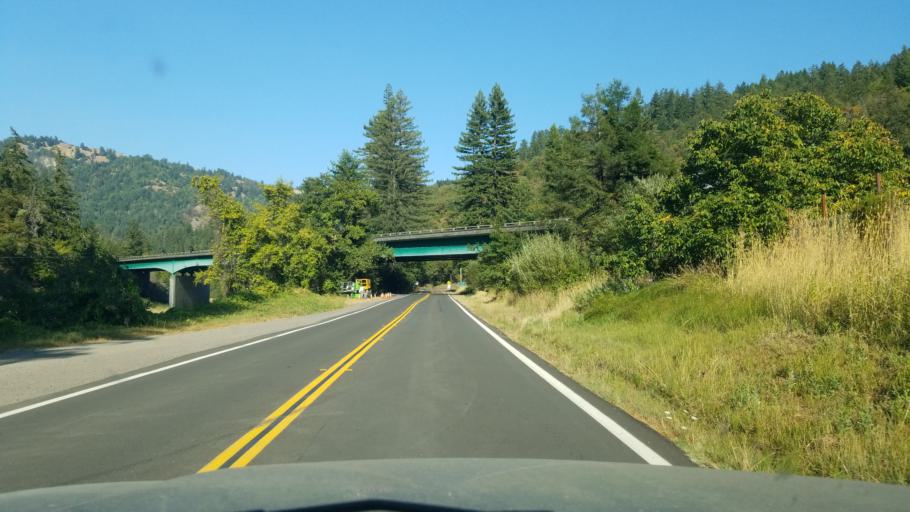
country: US
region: California
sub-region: Humboldt County
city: Redway
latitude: 40.1813
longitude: -123.7777
